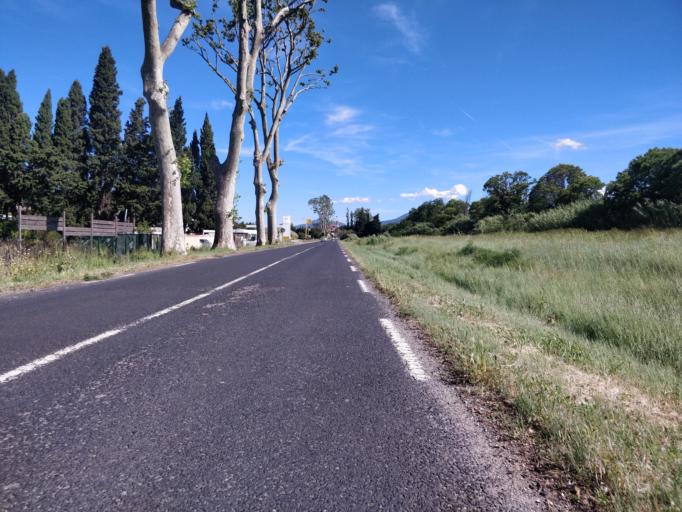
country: FR
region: Languedoc-Roussillon
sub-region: Departement des Pyrenees-Orientales
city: Corneilla-del-Vercol
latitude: 42.6117
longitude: 2.9604
